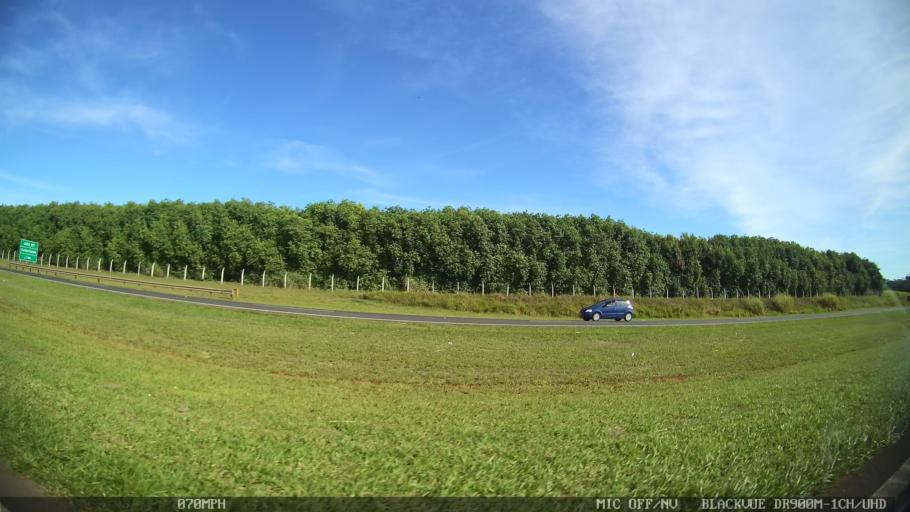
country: BR
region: Sao Paulo
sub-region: Cordeiropolis
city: Cordeiropolis
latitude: -22.4524
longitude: -47.3990
